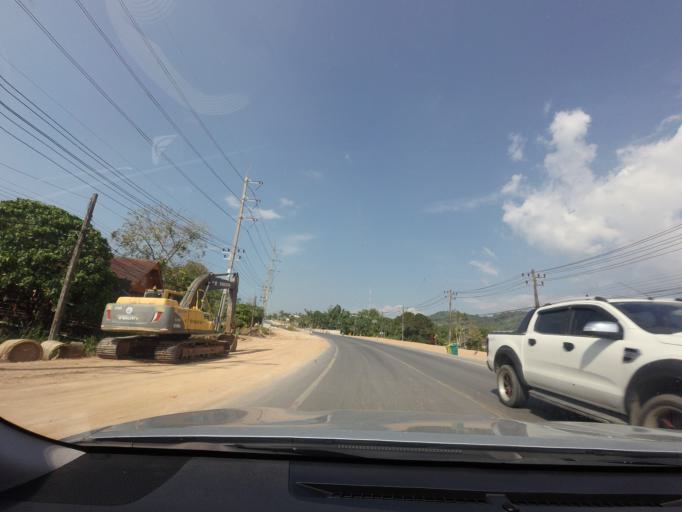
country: TH
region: Phangnga
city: Ban Khao Lak
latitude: 8.7012
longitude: 98.2583
